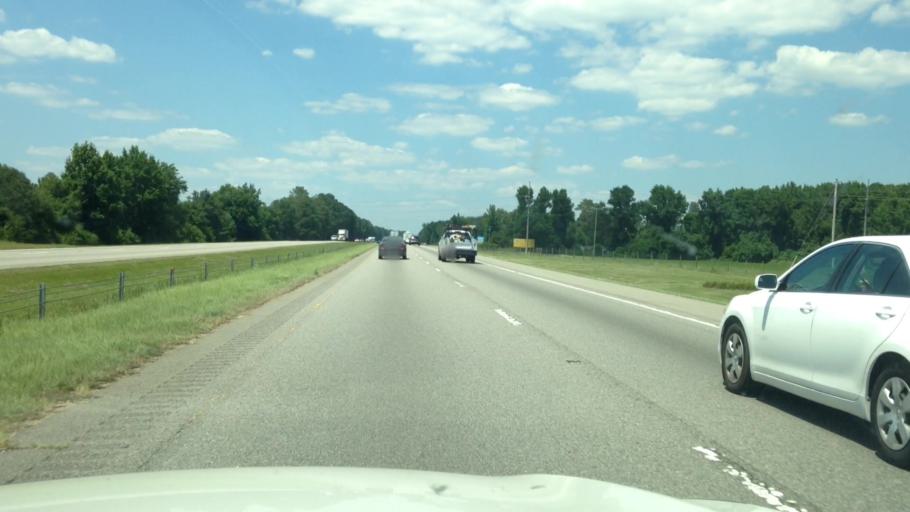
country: US
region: North Carolina
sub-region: Cumberland County
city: Hope Mills
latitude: 34.8911
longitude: -78.9598
